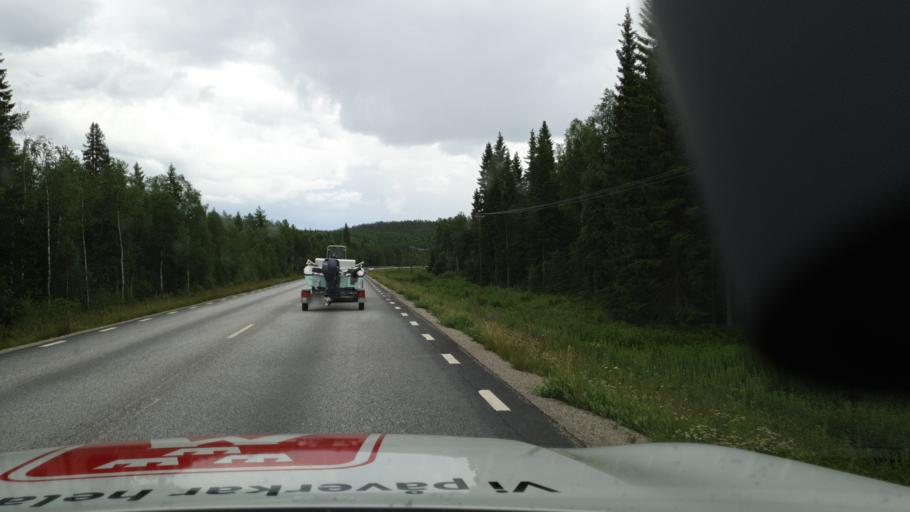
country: SE
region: Vaesterbotten
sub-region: Vannas Kommun
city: Vaennaes
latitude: 64.0467
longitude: 19.6821
